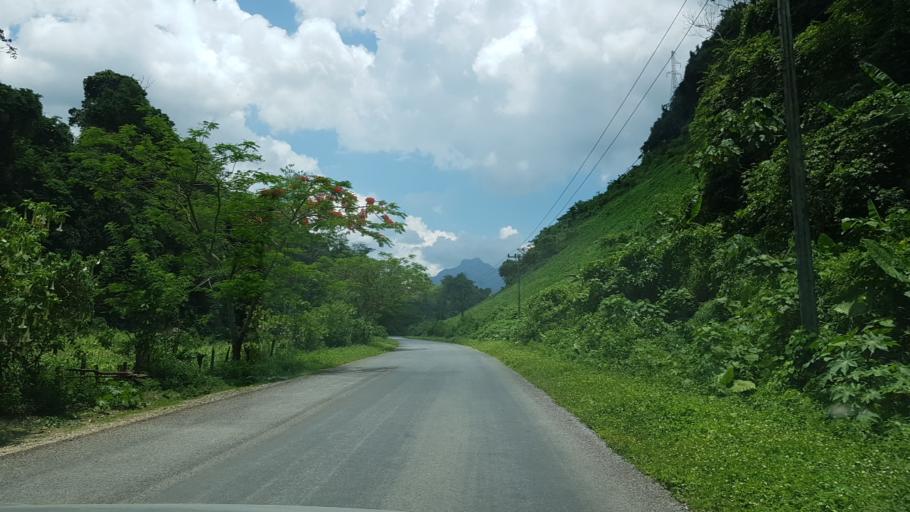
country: LA
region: Vientiane
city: Muang Kasi
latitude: 19.1390
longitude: 102.2982
